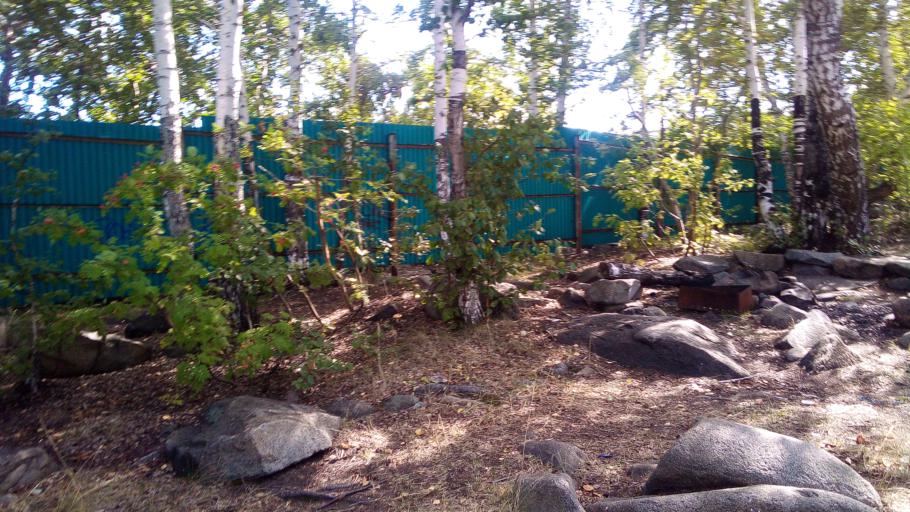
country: RU
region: Chelyabinsk
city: Tayginka
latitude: 55.4806
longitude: 60.4976
